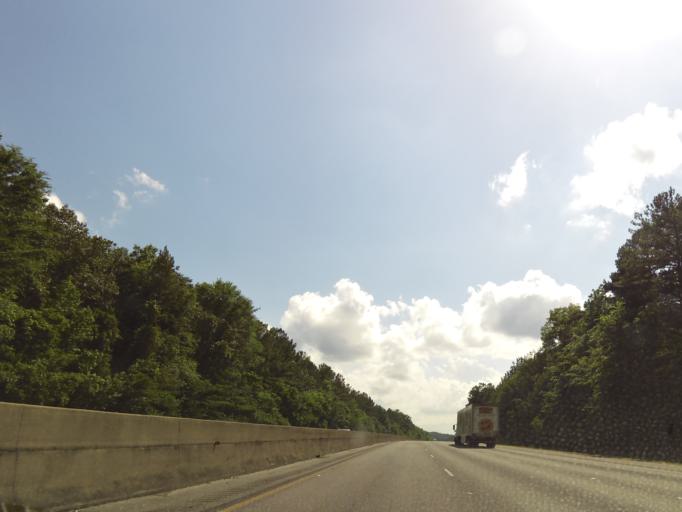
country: US
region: Alabama
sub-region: Jefferson County
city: Leeds
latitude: 33.5521
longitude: -86.5760
